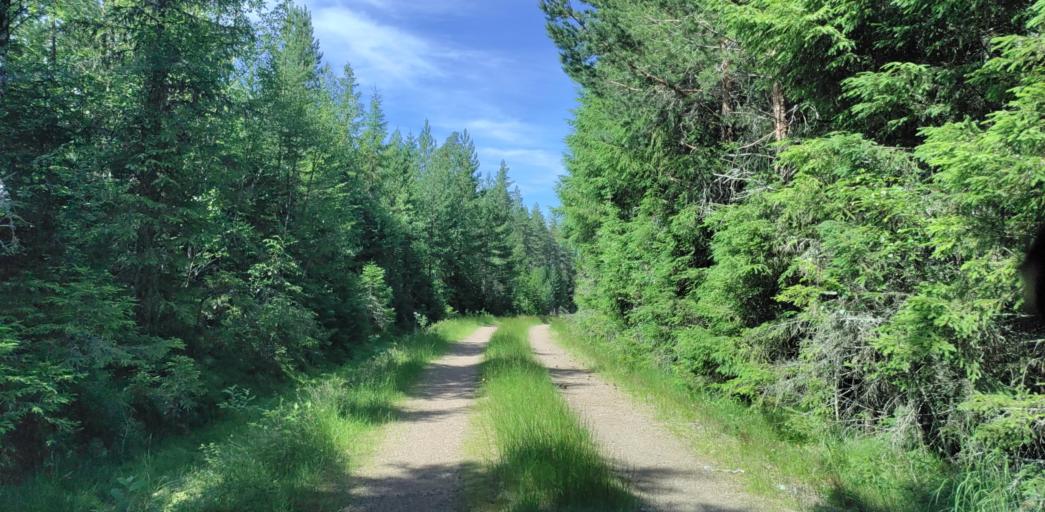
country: SE
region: Vaermland
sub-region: Hagfors Kommun
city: Ekshaerad
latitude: 60.0935
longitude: 13.3746
